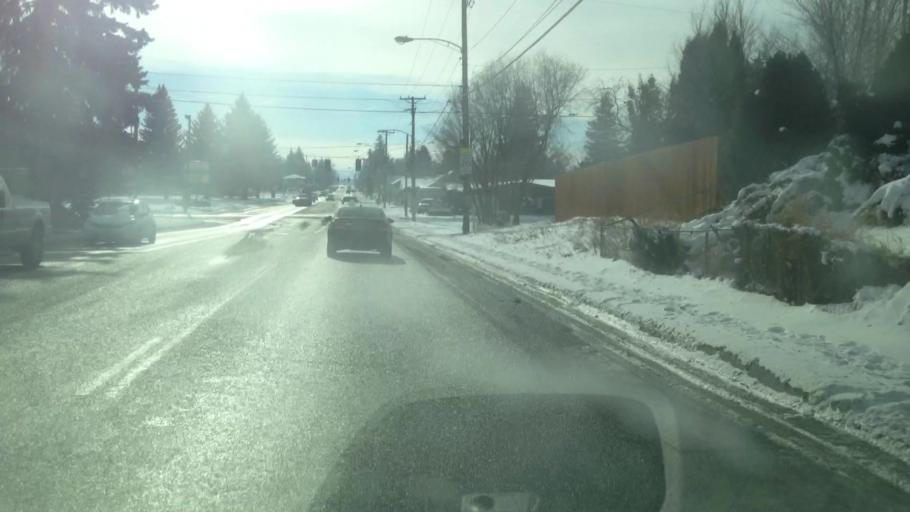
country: US
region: Idaho
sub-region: Bonneville County
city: Idaho Falls
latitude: 43.4941
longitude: -112.0239
